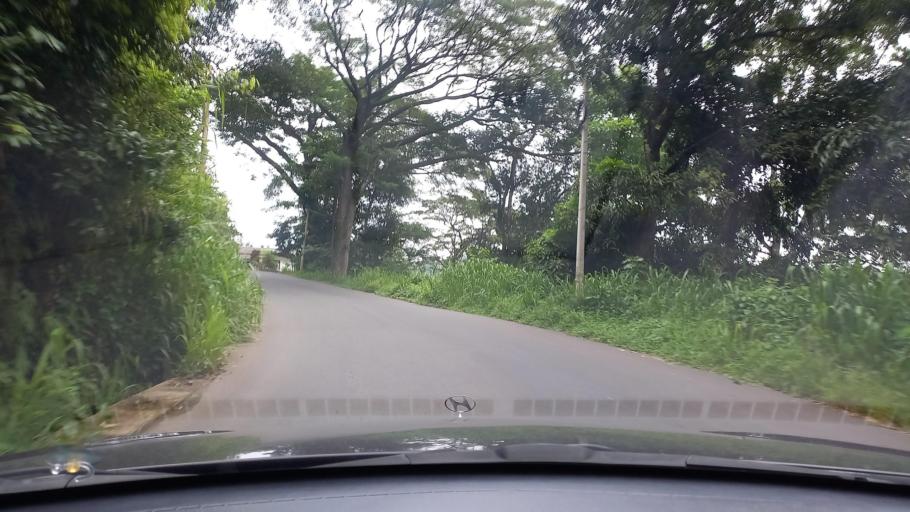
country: LK
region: Central
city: Kandy
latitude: 7.2350
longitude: 80.6034
